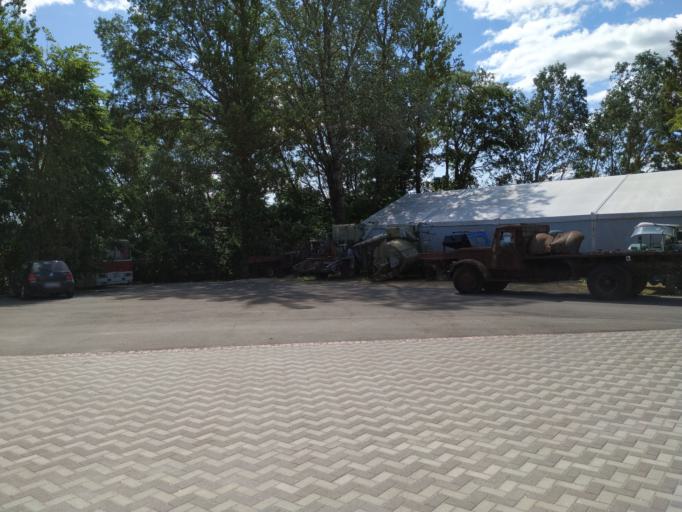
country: LT
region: Panevezys
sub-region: Birzai
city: Birzai
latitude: 56.2887
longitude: 24.6444
